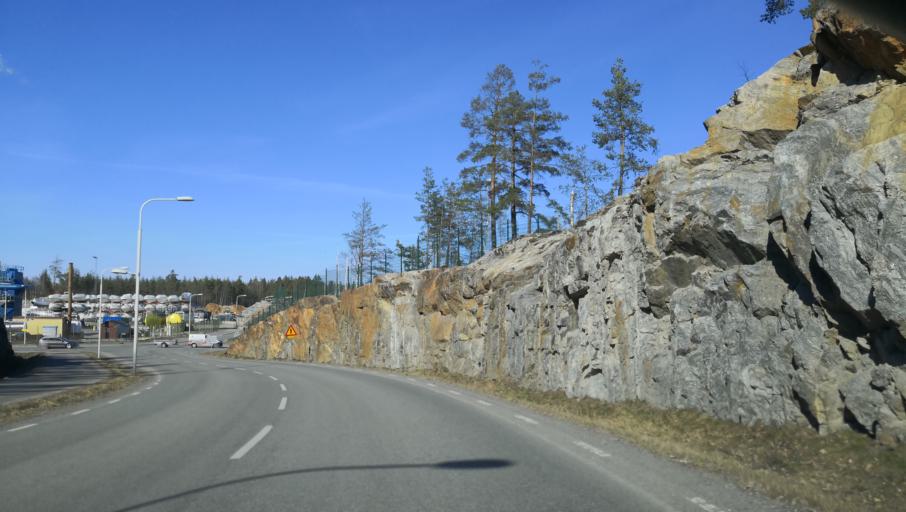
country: SE
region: Stockholm
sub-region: Varmdo Kommun
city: Gustavsberg
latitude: 59.3118
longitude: 18.3792
